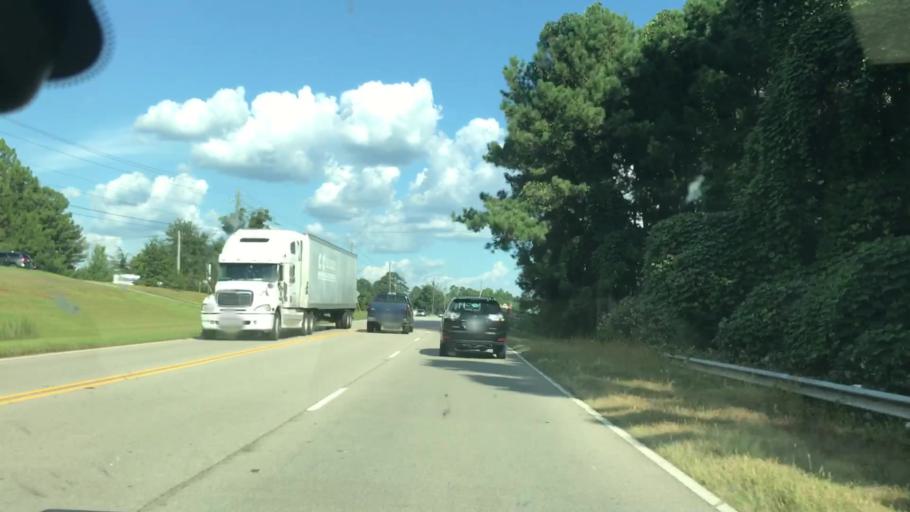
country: US
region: Georgia
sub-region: Troup County
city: La Grange
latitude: 32.9625
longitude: -84.9790
